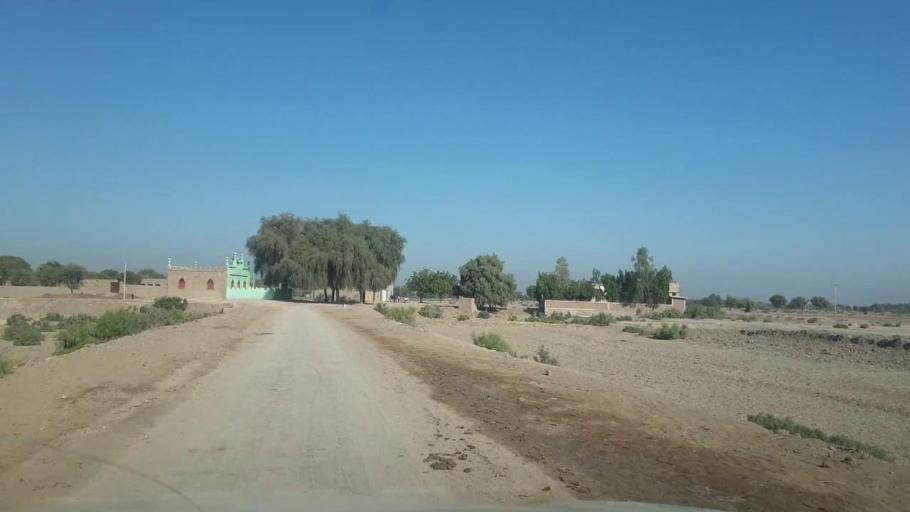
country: PK
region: Sindh
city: Bhan
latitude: 26.5475
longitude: 67.6561
